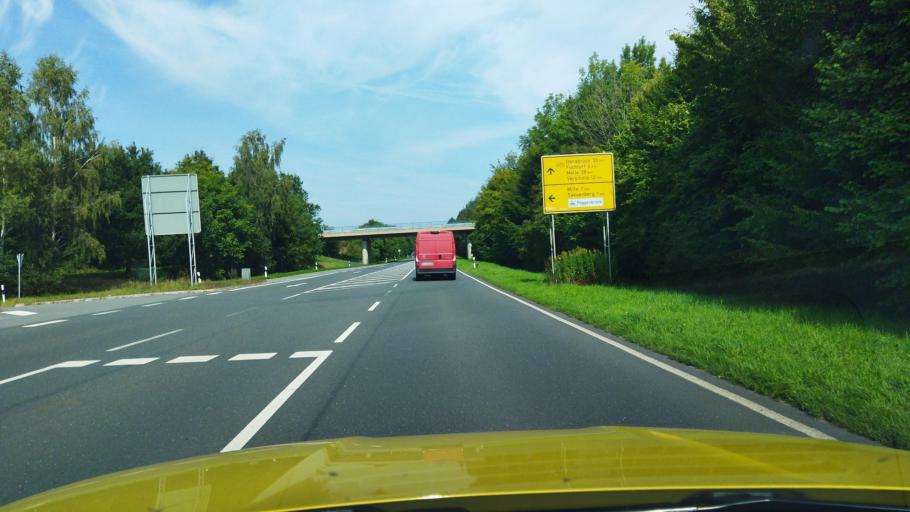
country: DE
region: North Rhine-Westphalia
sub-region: Regierungsbezirk Munster
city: Sassenberg
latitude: 51.9932
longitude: 8.0315
